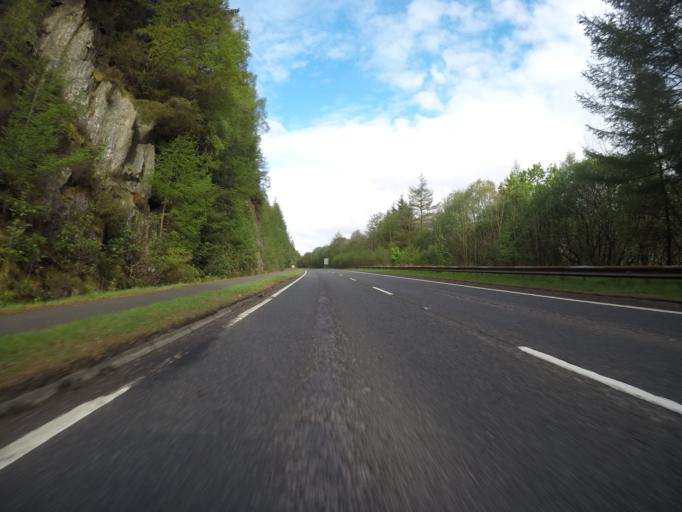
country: GB
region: Scotland
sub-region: Highland
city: Fort William
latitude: 56.6807
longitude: -5.1609
